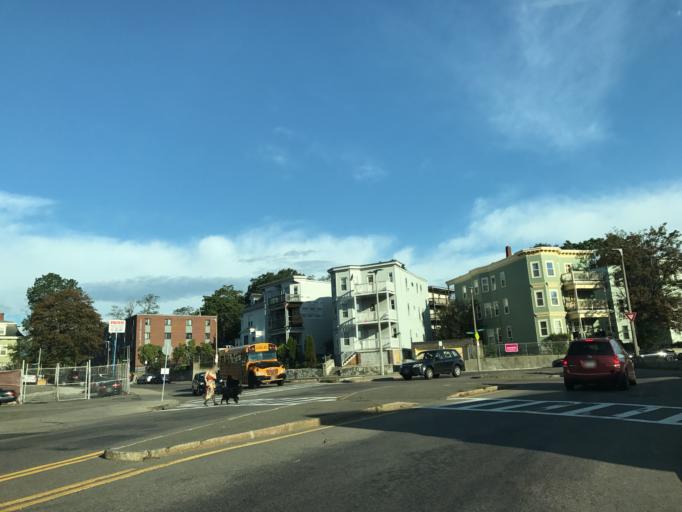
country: US
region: Massachusetts
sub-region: Suffolk County
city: South Boston
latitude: 42.3096
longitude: -71.0601
